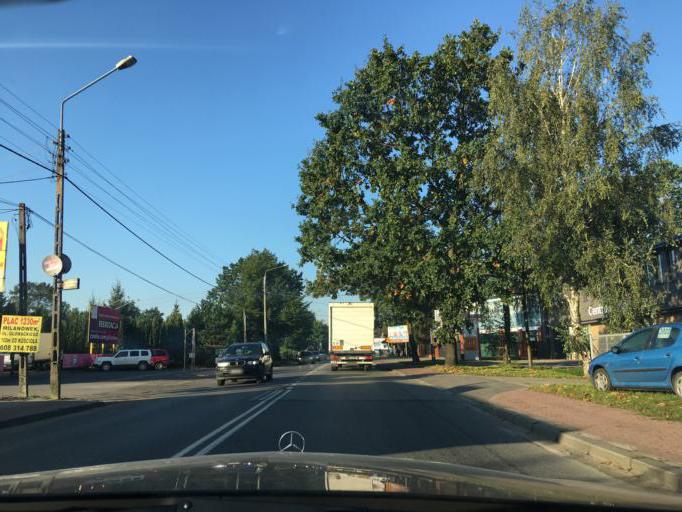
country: PL
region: Masovian Voivodeship
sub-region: Powiat grodziski
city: Milanowek
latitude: 52.1237
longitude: 20.6843
